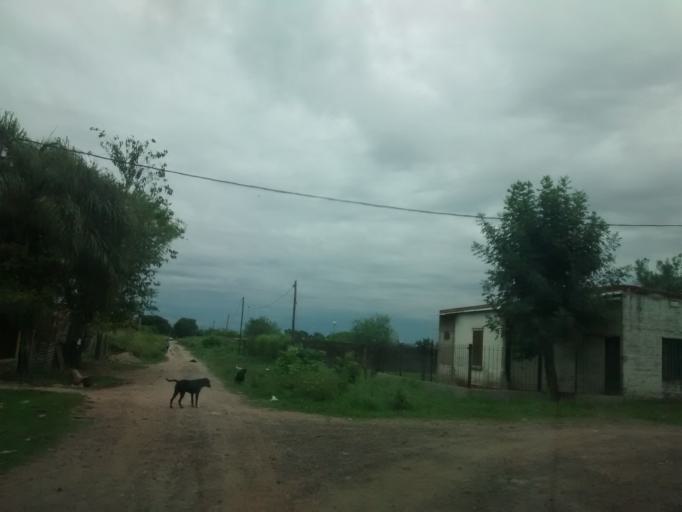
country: AR
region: Chaco
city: Puerto Tirol
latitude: -27.3765
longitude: -59.0986
